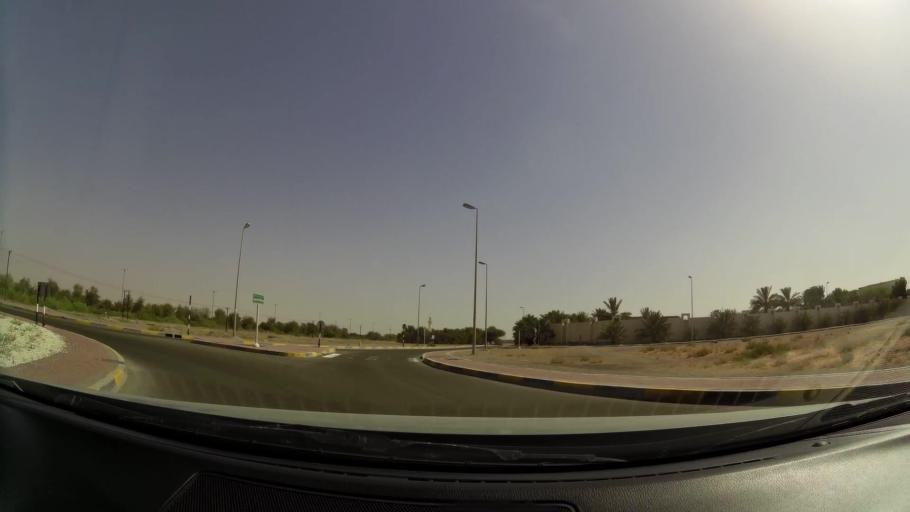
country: OM
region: Al Buraimi
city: Al Buraymi
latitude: 24.3035
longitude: 55.7939
